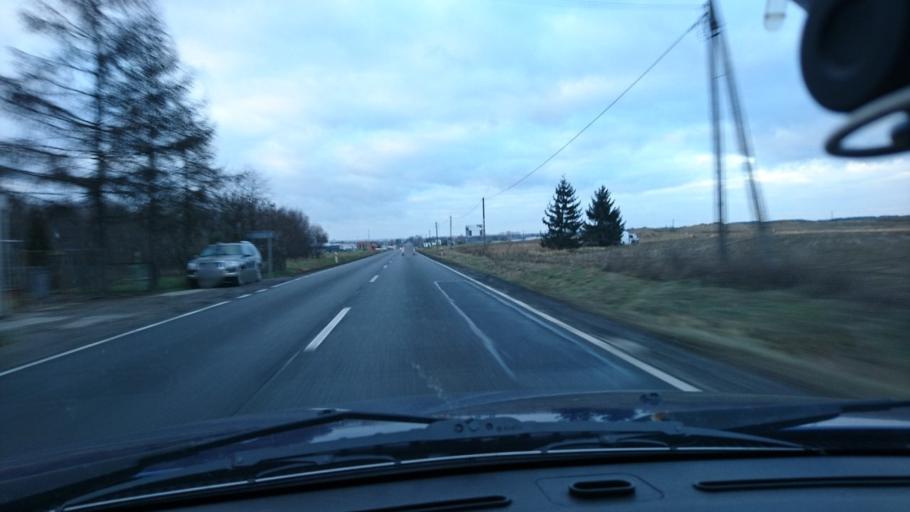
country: PL
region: Greater Poland Voivodeship
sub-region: Powiat kepinski
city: Baranow
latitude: 51.2546
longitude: 18.0118
